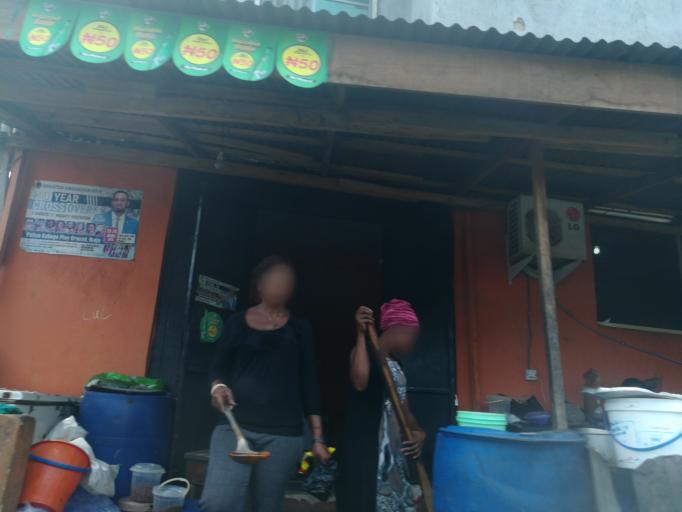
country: NG
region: Lagos
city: Ojota
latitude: 6.5720
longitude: 3.3640
